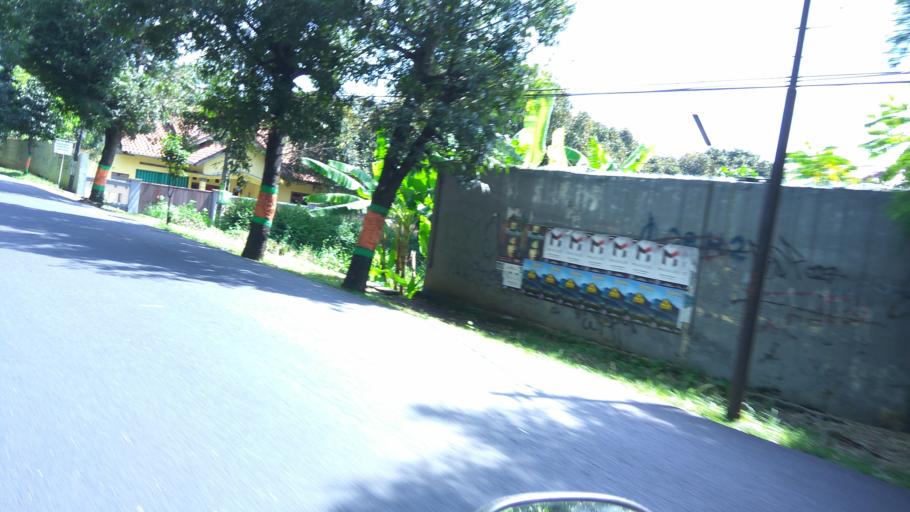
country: ID
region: Central Java
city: Ungaran
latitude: -7.1163
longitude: 110.4078
